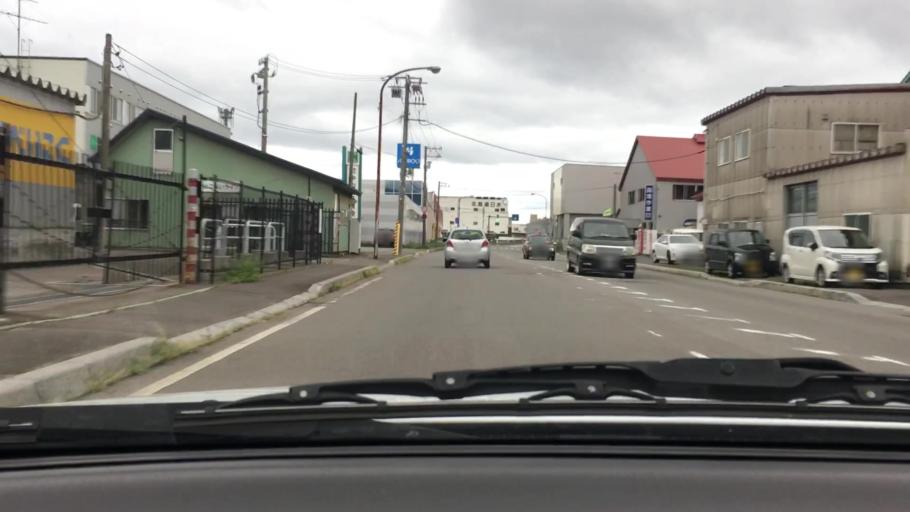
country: JP
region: Hokkaido
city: Hakodate
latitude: 41.7878
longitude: 140.7282
